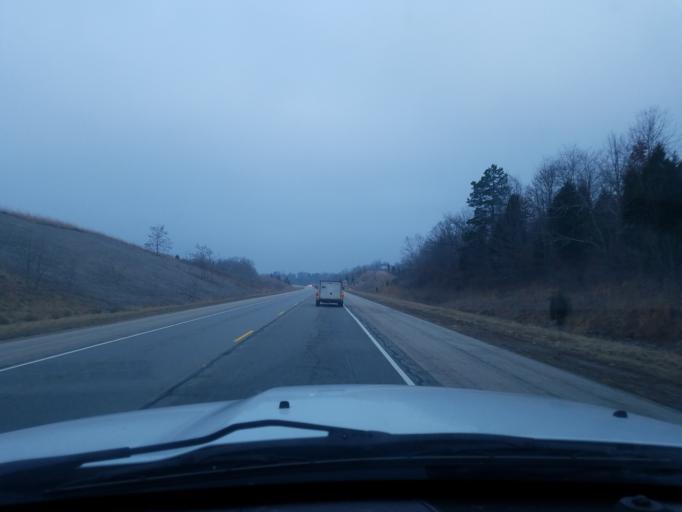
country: US
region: Indiana
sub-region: Perry County
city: Tell City
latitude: 38.0463
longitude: -86.6466
